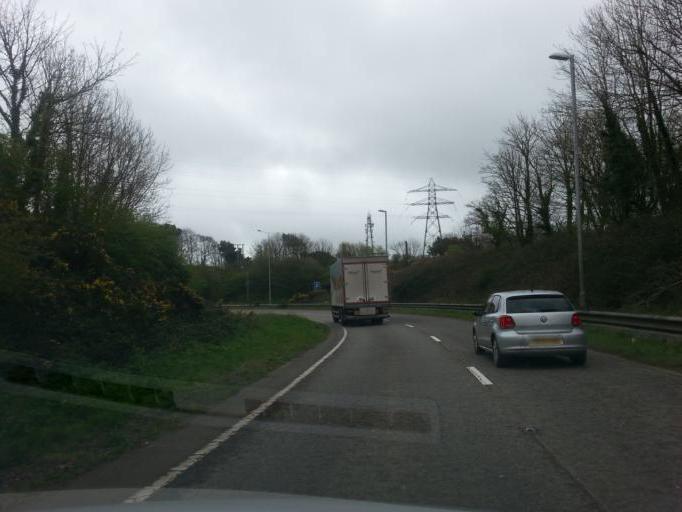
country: GB
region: England
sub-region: Cornwall
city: Camborne
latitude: 50.2303
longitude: -5.2817
